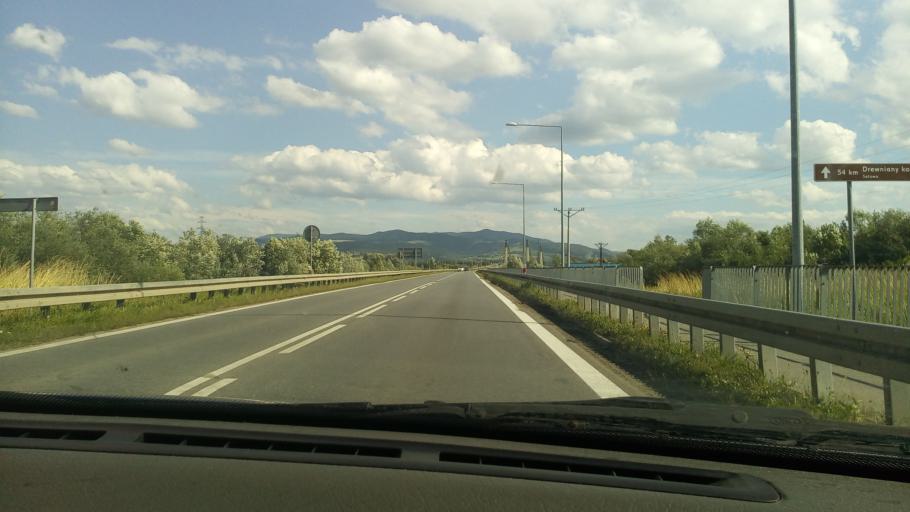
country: PL
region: Lesser Poland Voivodeship
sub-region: Powiat nowosadecki
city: Stary Sacz
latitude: 49.5892
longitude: 20.6314
